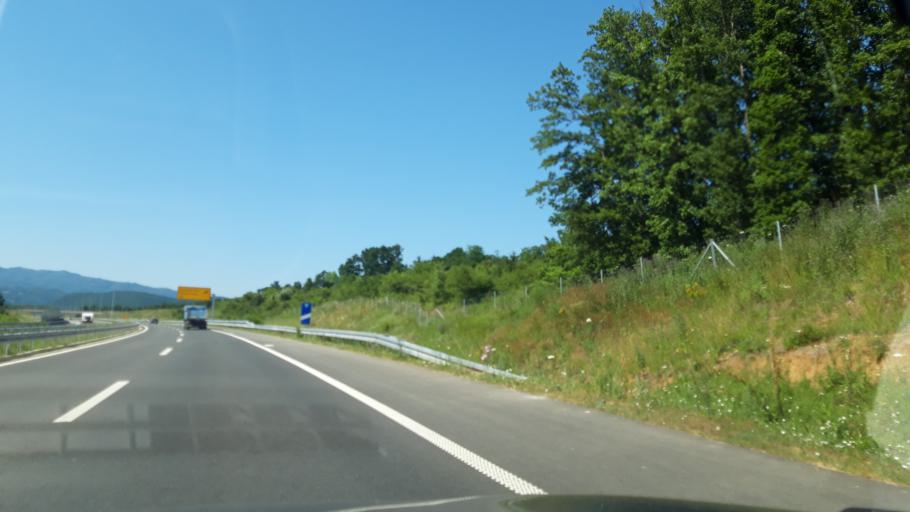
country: RS
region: Central Serbia
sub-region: Pcinjski Okrug
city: Vladicin Han
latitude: 42.6984
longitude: 22.0762
